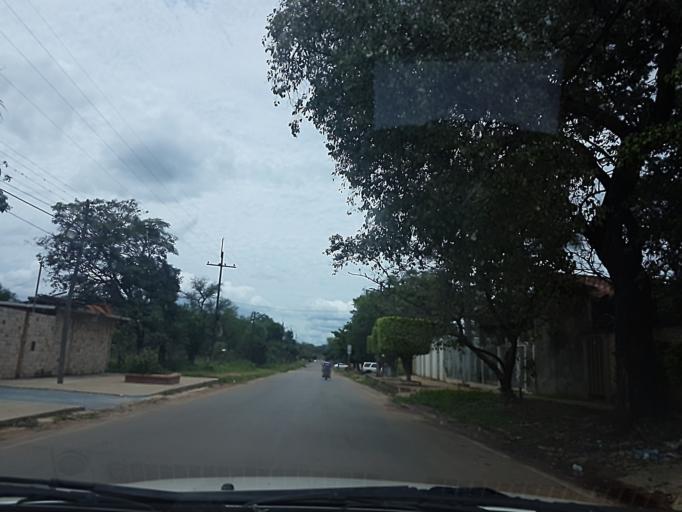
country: PY
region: Central
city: Colonia Mariano Roque Alonso
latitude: -25.1878
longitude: -57.5258
